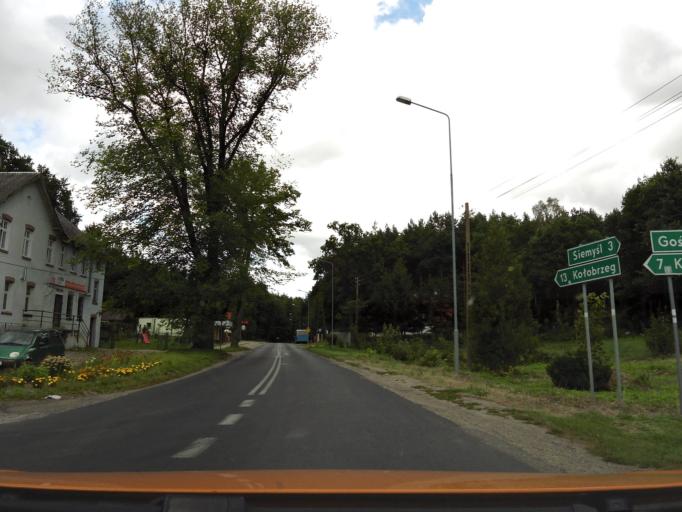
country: PL
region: West Pomeranian Voivodeship
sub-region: Powiat kolobrzeski
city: Goscino
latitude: 54.0557
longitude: 15.5505
